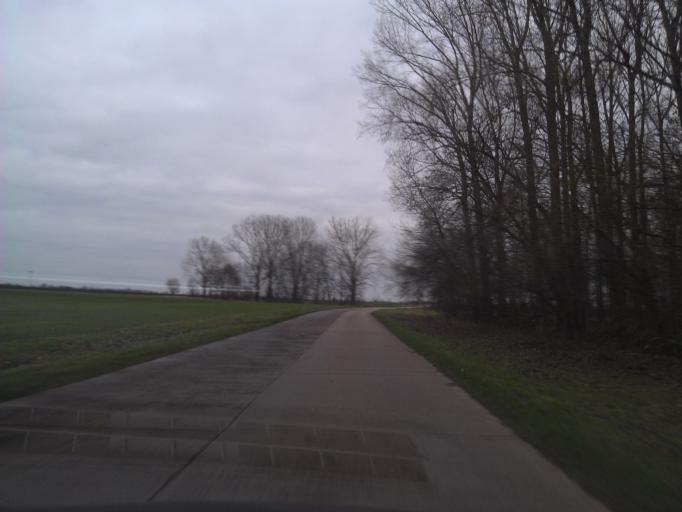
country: DE
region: Thuringia
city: Pferdingsleben
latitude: 50.9726
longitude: 10.8241
